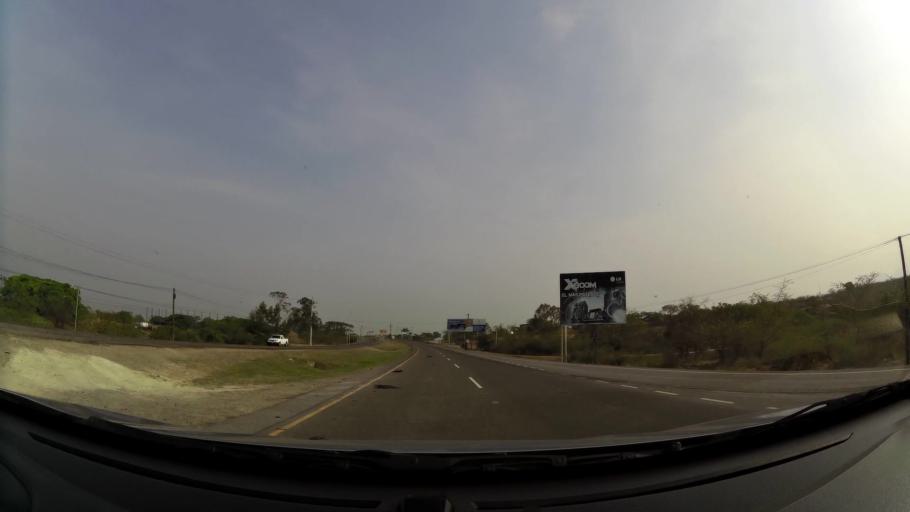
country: HN
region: Comayagua
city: Comayagua
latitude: 14.4163
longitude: -87.6249
